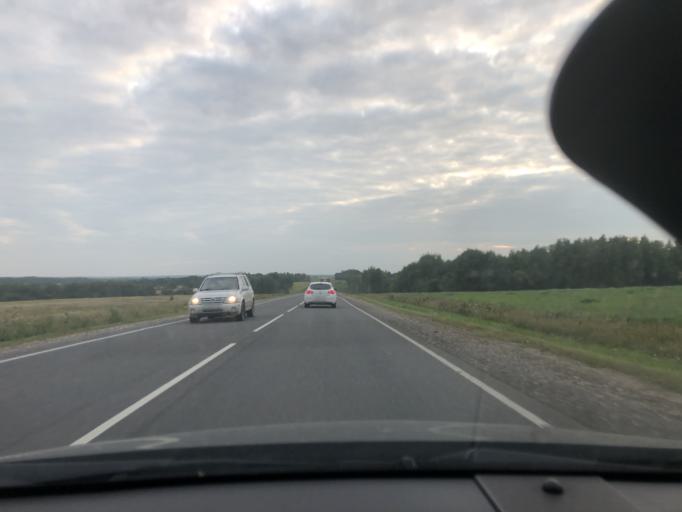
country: RU
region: Kaluga
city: Ferzikovo
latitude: 54.3474
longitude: 36.8521
